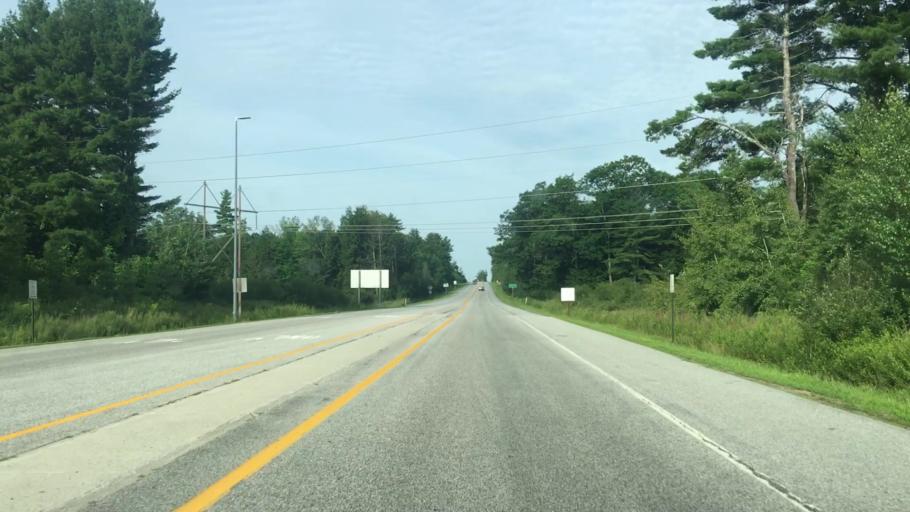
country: US
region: Maine
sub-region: Cumberland County
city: Gorham
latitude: 43.6518
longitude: -70.4287
